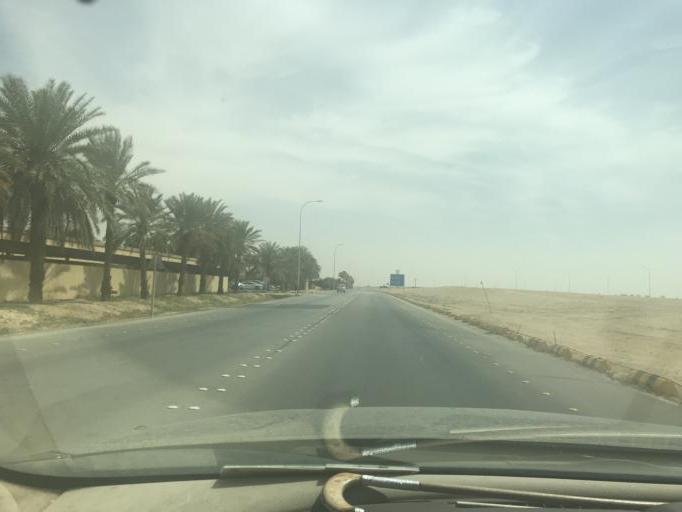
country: SA
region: Ar Riyad
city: Riyadh
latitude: 24.9757
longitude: 46.6886
